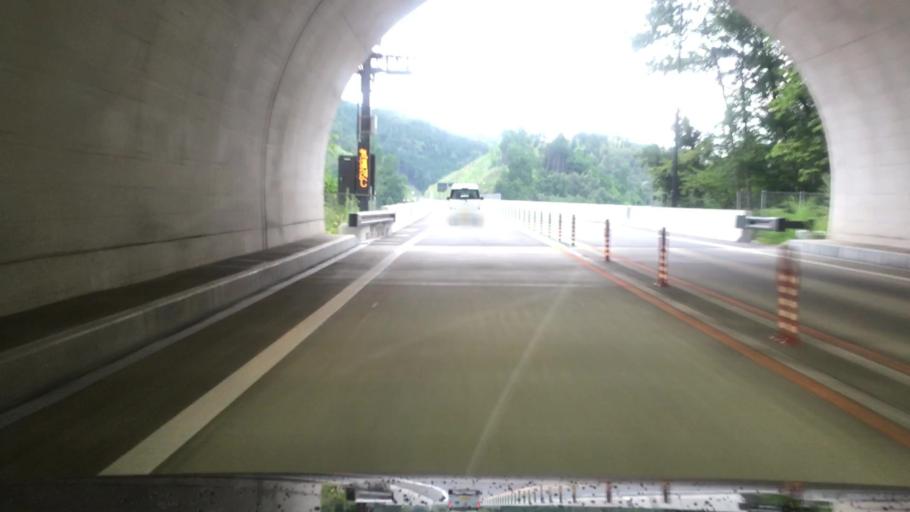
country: JP
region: Hyogo
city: Toyooka
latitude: 35.4366
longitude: 134.7678
